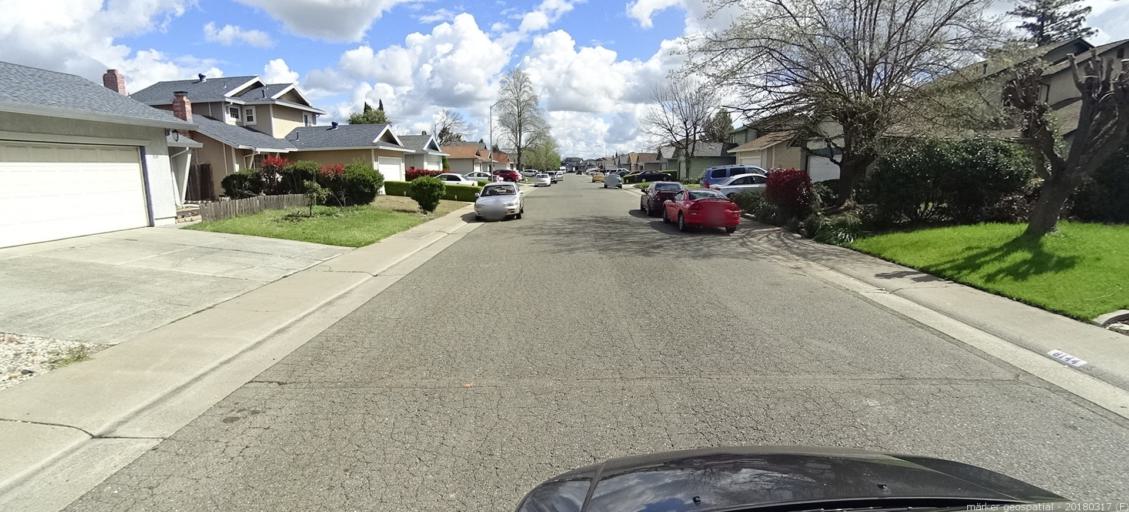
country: US
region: California
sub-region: Sacramento County
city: Florin
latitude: 38.4748
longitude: -121.4071
